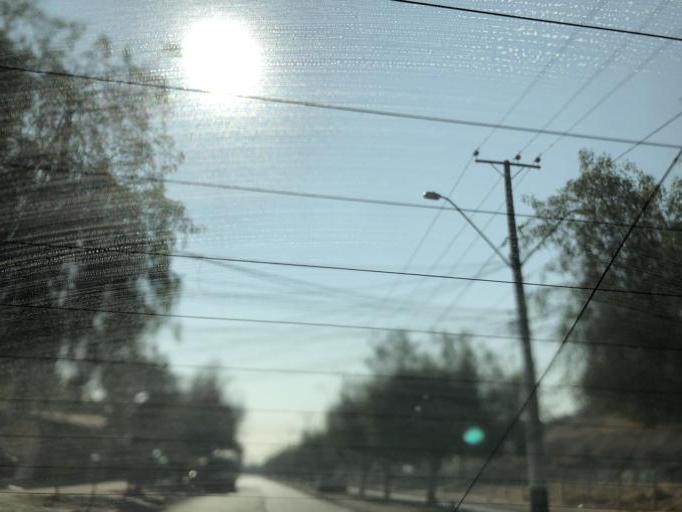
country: CL
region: Santiago Metropolitan
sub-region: Provincia de Cordillera
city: Puente Alto
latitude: -33.5999
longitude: -70.5566
